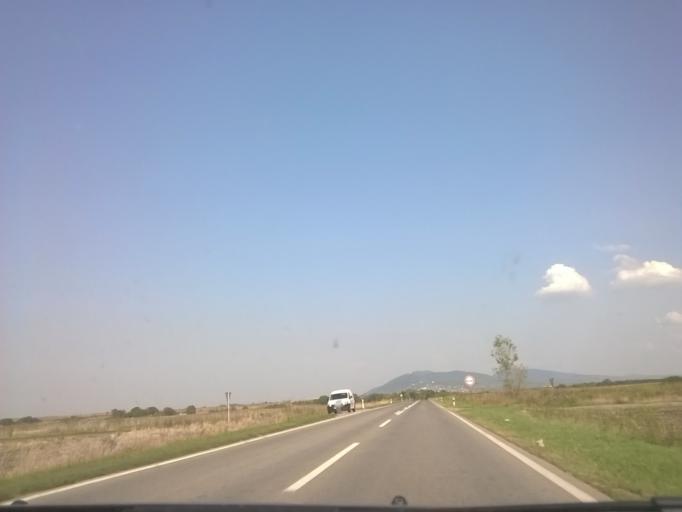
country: RS
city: Pavlis
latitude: 45.0847
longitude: 21.2412
